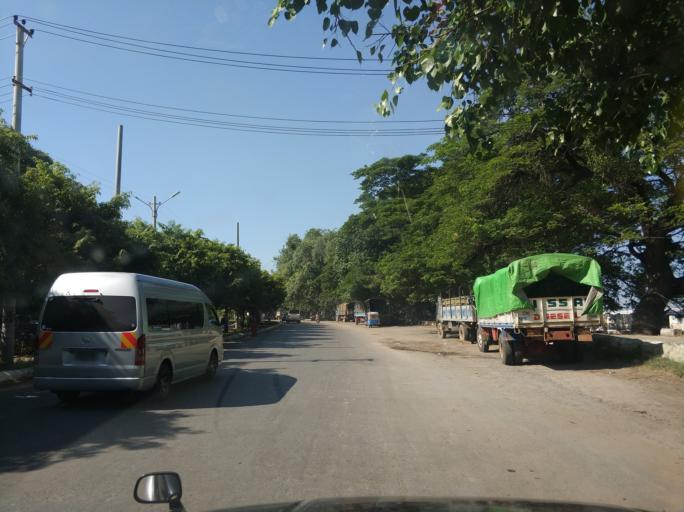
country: MM
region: Mandalay
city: Mandalay
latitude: 21.9701
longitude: 96.0563
